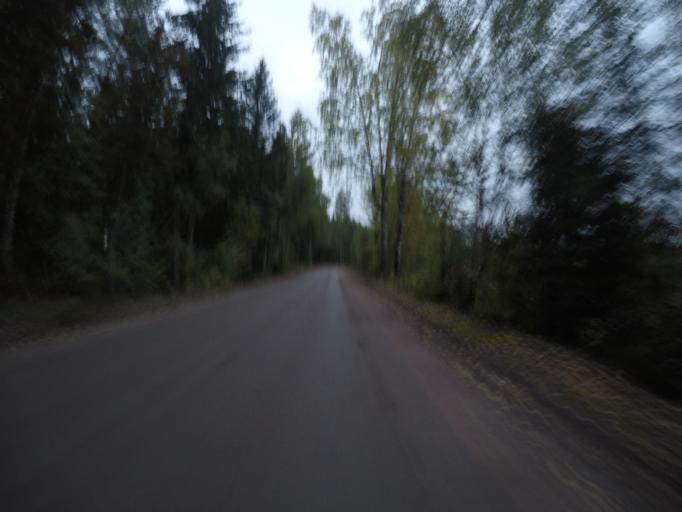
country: SE
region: Vaestmanland
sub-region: Kungsors Kommun
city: Kungsoer
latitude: 59.3882
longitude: 16.1168
